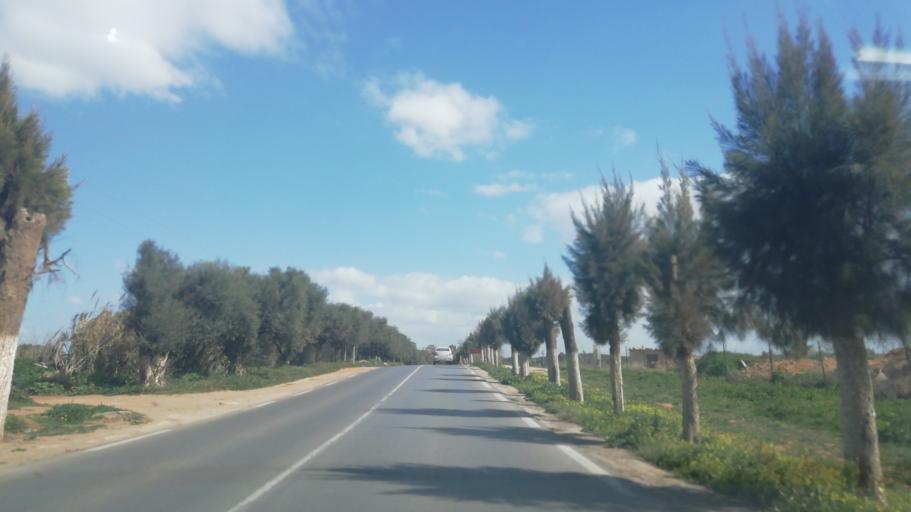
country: DZ
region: Mostaganem
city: Mostaganem
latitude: 35.9992
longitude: 0.3119
